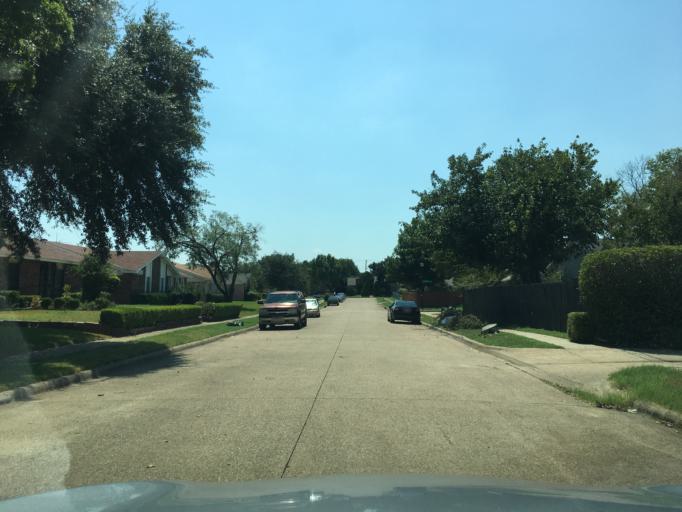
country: US
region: Texas
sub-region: Dallas County
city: Garland
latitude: 32.9539
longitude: -96.6690
